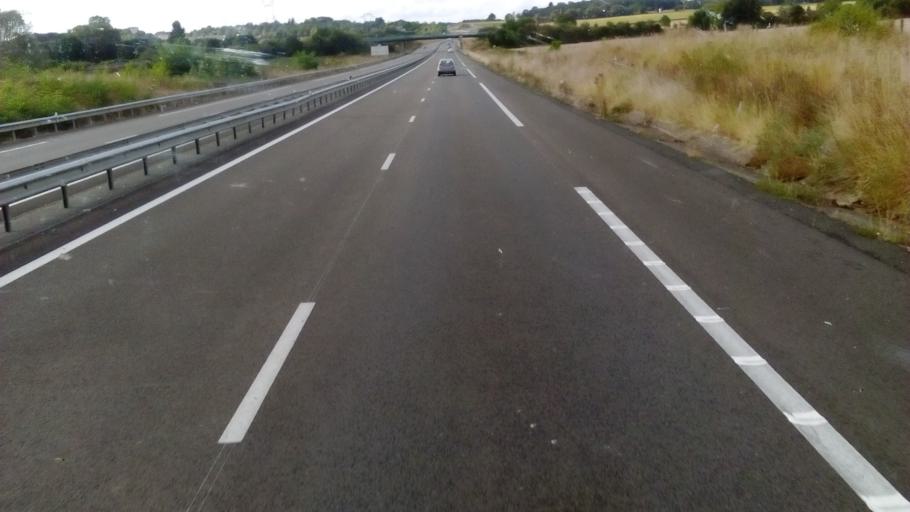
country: FR
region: Bourgogne
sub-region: Departement de la Nievre
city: Varennes-Vauzelles
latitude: 47.0296
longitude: 3.1606
